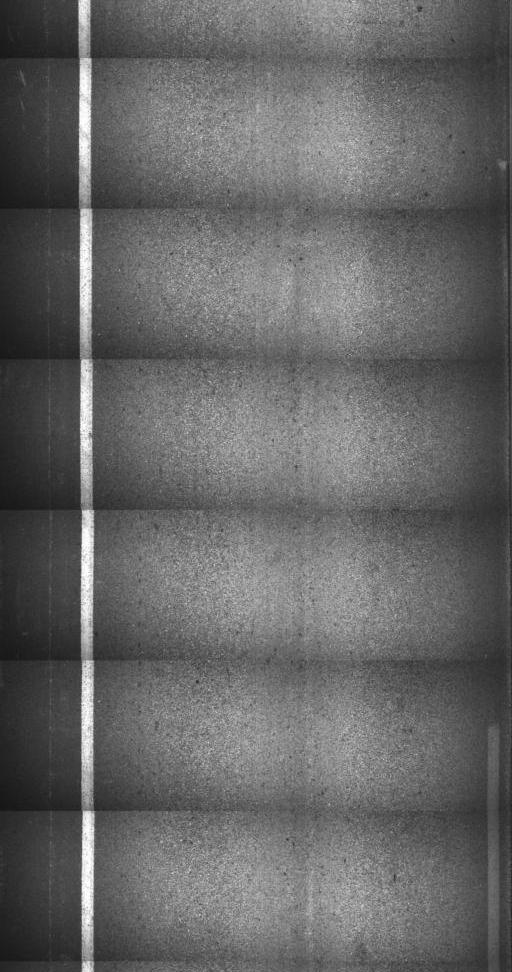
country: US
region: Vermont
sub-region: Addison County
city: Vergennes
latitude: 44.0595
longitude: -73.3025
